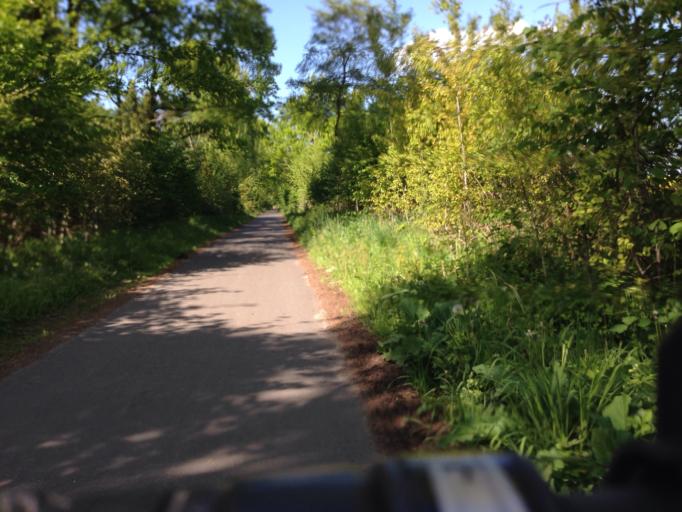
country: DE
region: Schleswig-Holstein
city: Braak
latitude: 53.6302
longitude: 10.2298
